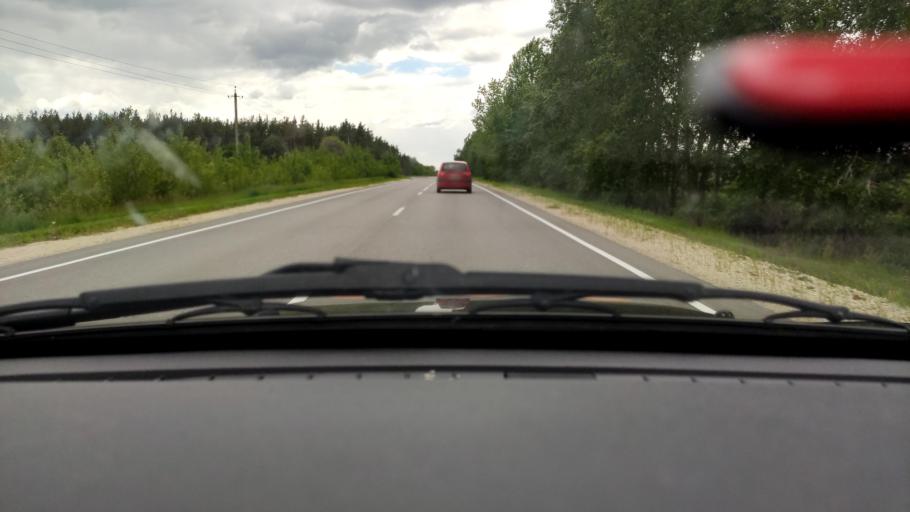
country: RU
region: Belgorod
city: Krasnoye
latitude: 51.0684
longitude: 38.7936
